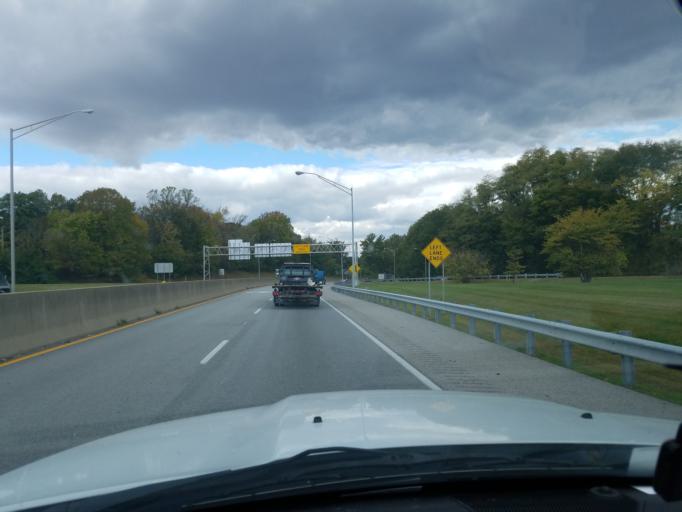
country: US
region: Kentucky
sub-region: Henderson County
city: Henderson
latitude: 37.8579
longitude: -87.5740
